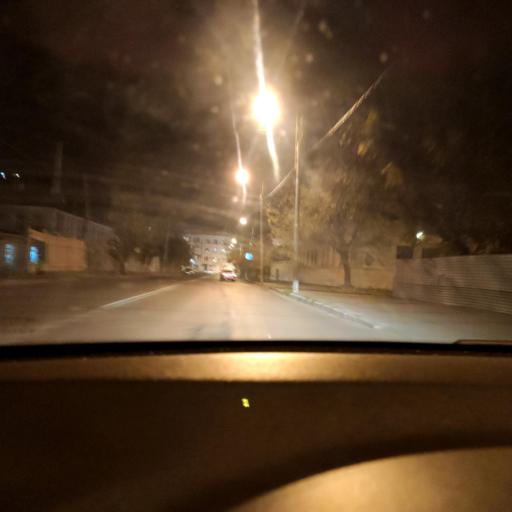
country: RU
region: Samara
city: Samara
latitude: 53.1986
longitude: 50.1333
